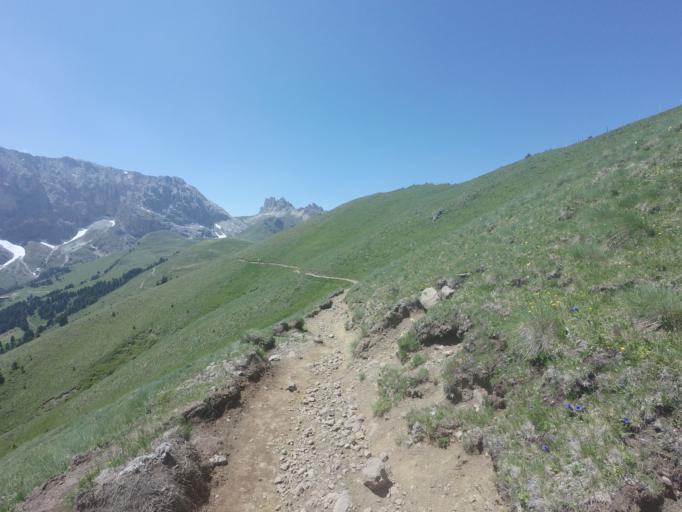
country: IT
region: Trentino-Alto Adige
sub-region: Provincia di Trento
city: Mazzin
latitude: 46.4988
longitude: 11.6728
